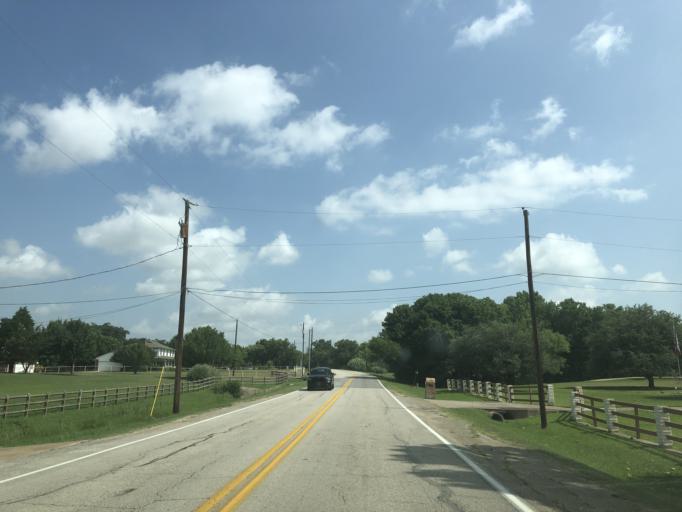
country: US
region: Texas
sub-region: Dallas County
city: Sunnyvale
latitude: 32.8230
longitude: -96.5595
